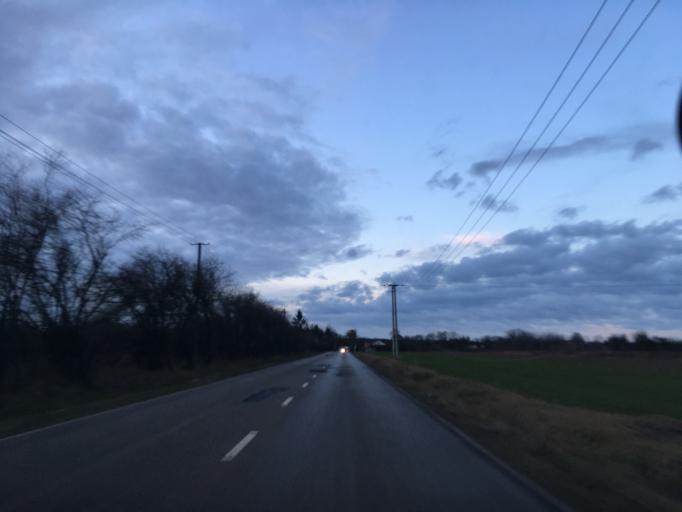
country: PL
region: Masovian Voivodeship
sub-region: Powiat pruszkowski
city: Owczarnia
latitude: 52.0782
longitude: 20.7053
